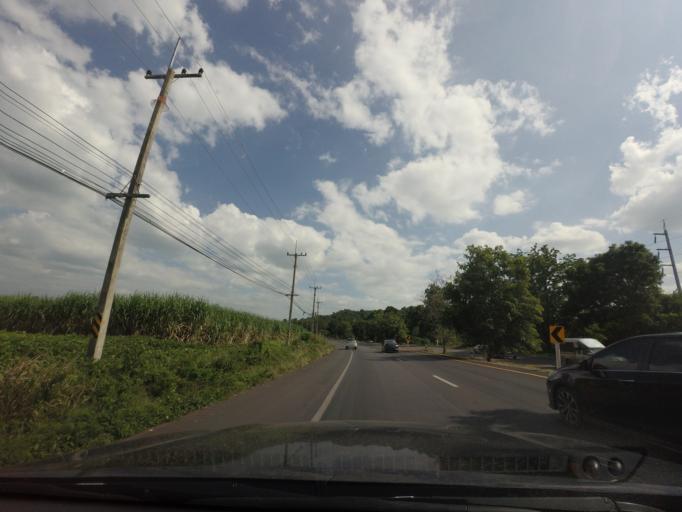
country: TH
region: Phetchabun
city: Wichian Buri
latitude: 15.6299
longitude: 101.0485
